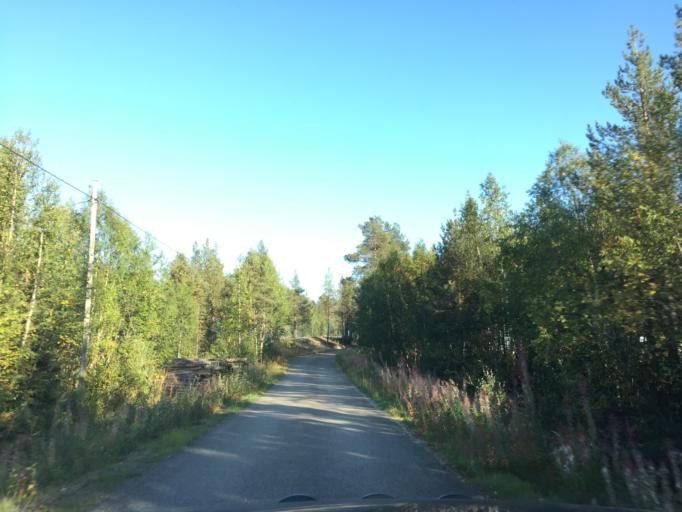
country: SE
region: Norrbotten
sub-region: Gallivare Kommun
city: Malmberget
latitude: 67.6547
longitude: 21.0356
